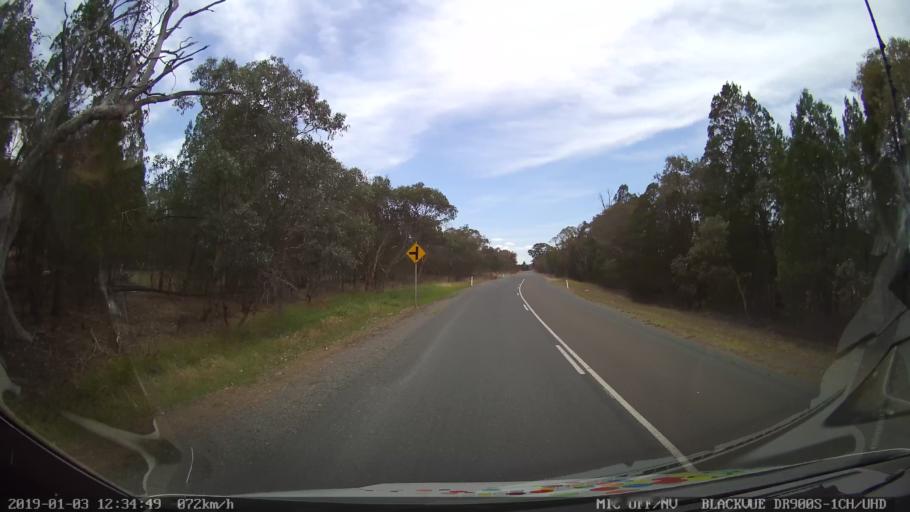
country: AU
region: New South Wales
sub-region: Weddin
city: Grenfell
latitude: -33.8725
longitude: 148.1666
